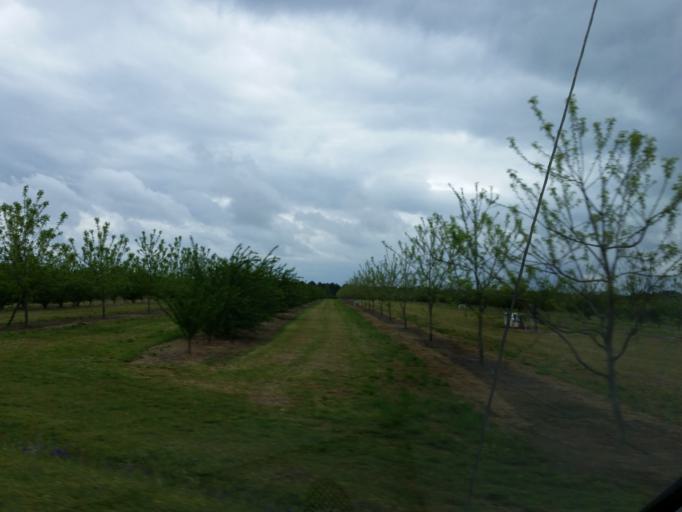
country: US
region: Georgia
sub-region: Peach County
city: Byron
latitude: 32.6693
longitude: -83.8337
